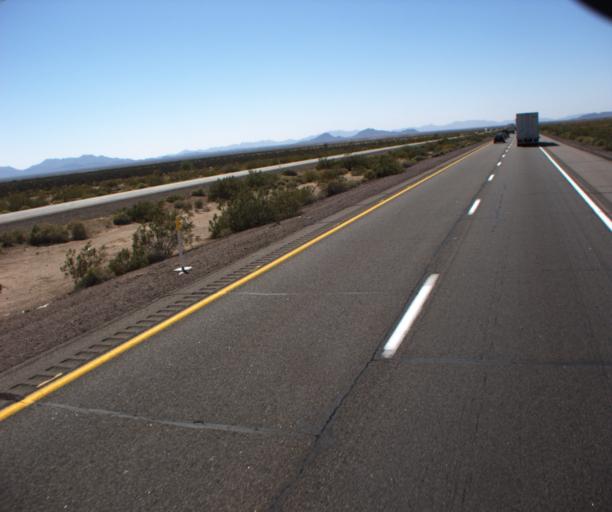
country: US
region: Arizona
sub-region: Yuma County
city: Wellton
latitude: 32.7169
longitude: -113.8007
